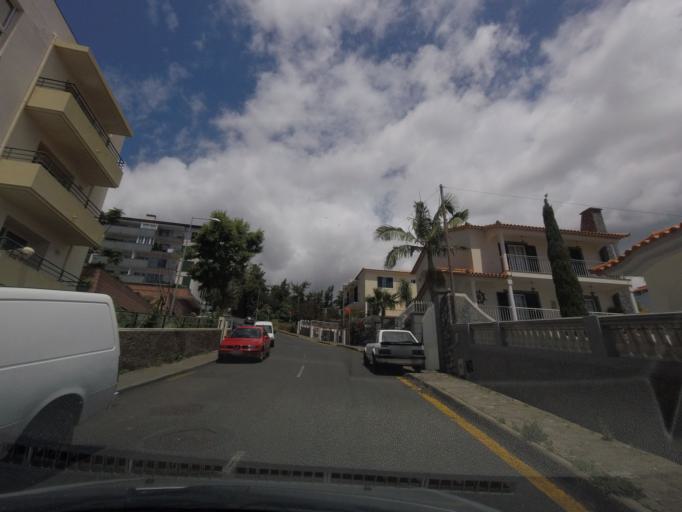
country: PT
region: Madeira
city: Canico
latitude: 32.6443
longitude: -16.8376
